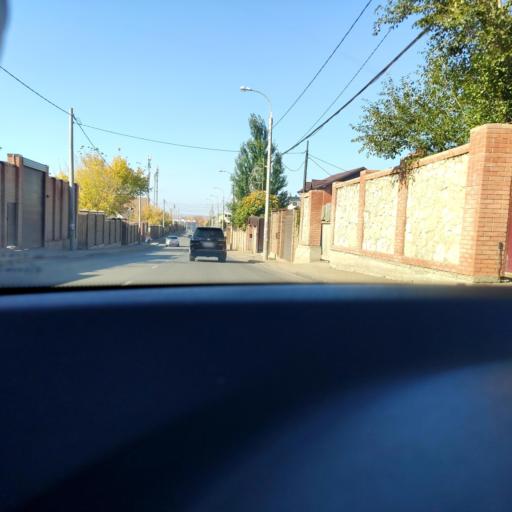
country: RU
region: Samara
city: Samara
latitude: 53.2665
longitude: 50.2044
